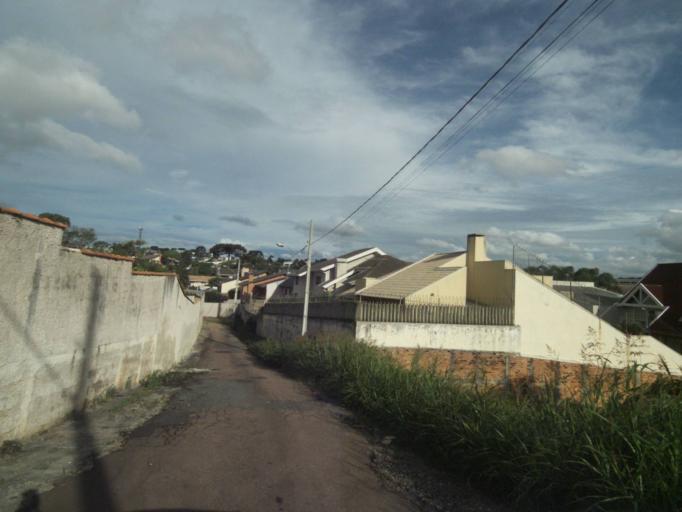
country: BR
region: Parana
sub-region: Curitiba
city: Curitiba
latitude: -25.4441
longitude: -49.3083
